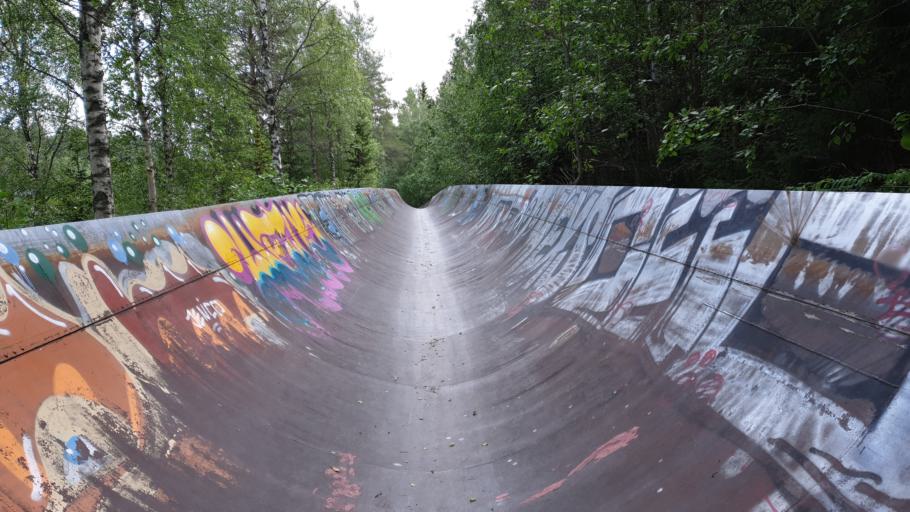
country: SE
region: Vaesterbotten
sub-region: Umea Kommun
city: Roback
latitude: 63.8335
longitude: 20.1241
